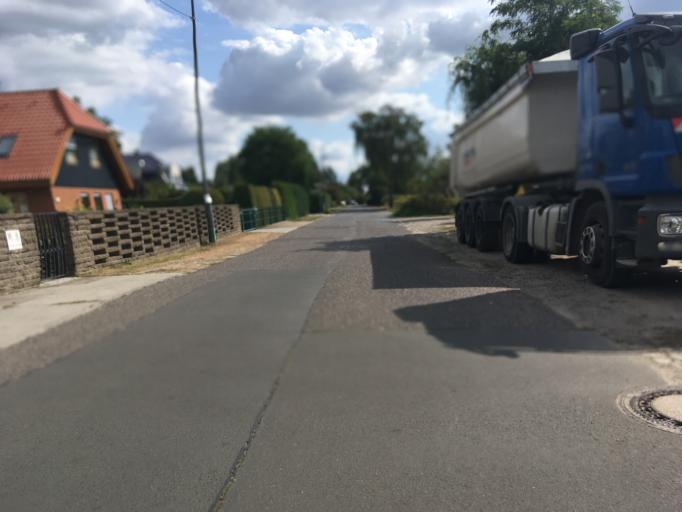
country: DE
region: Berlin
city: Karow
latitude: 52.6097
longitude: 13.4902
